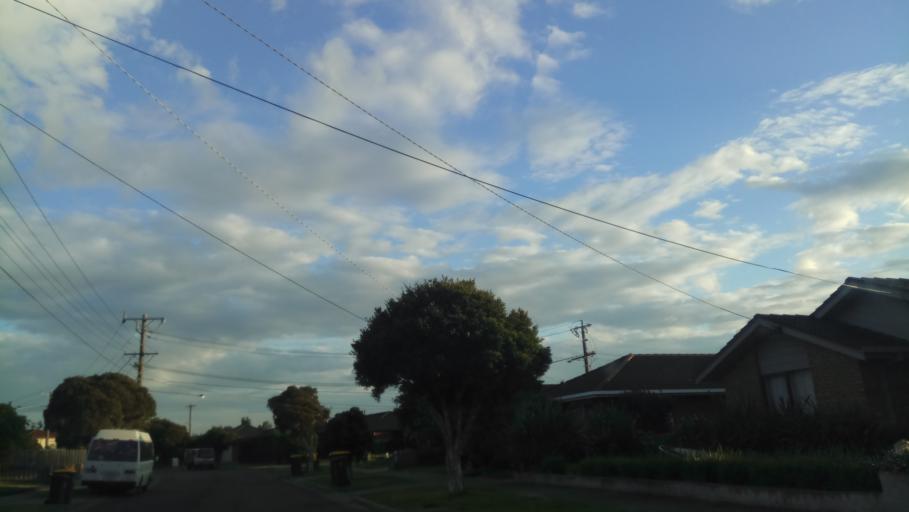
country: AU
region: Victoria
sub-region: Hobsons Bay
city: Altona Meadows
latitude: -37.8870
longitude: 144.7803
